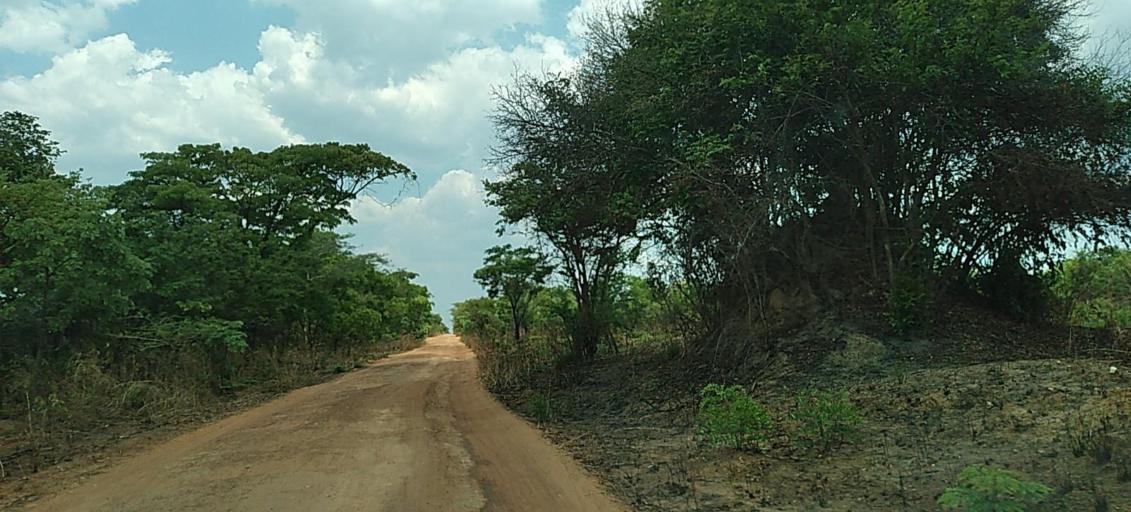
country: ZM
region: Copperbelt
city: Luanshya
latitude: -13.3790
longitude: 28.4325
